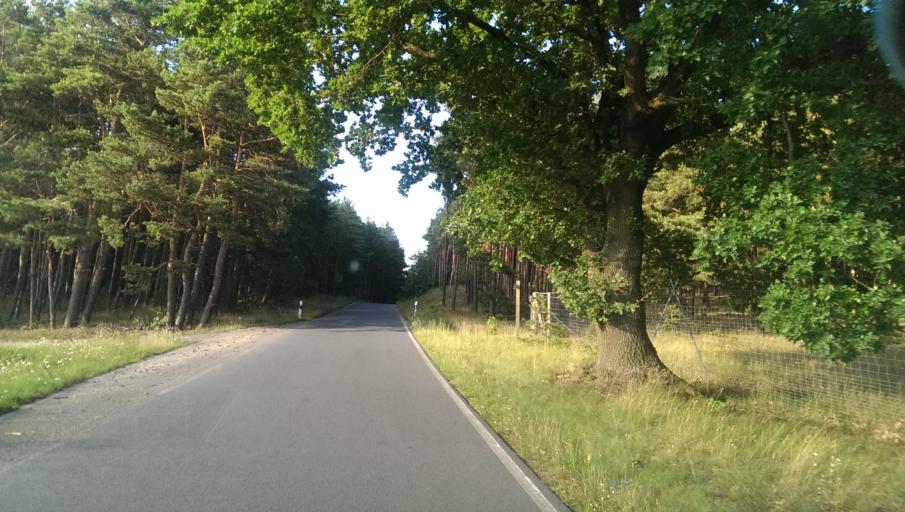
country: DE
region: Brandenburg
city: Treuenbrietzen
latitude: 52.0430
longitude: 12.8679
